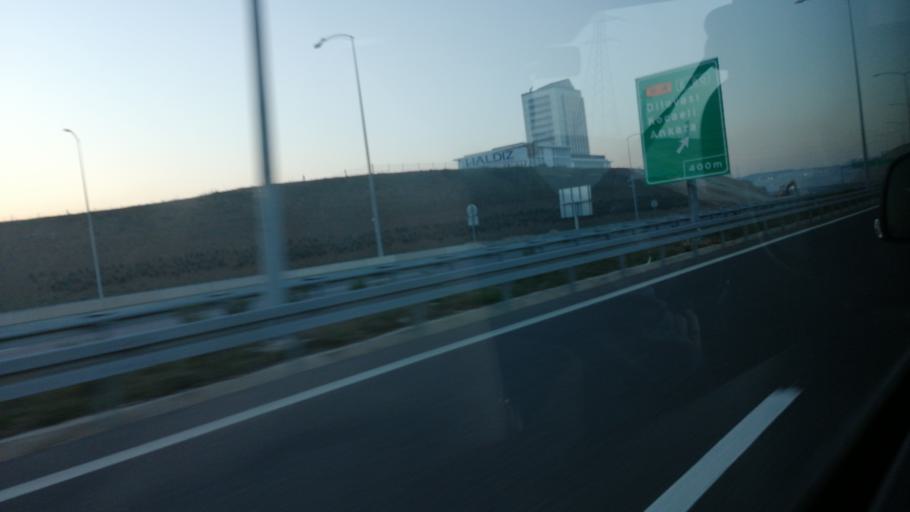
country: TR
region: Kocaeli
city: Tavsanli
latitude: 40.7895
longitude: 29.5143
